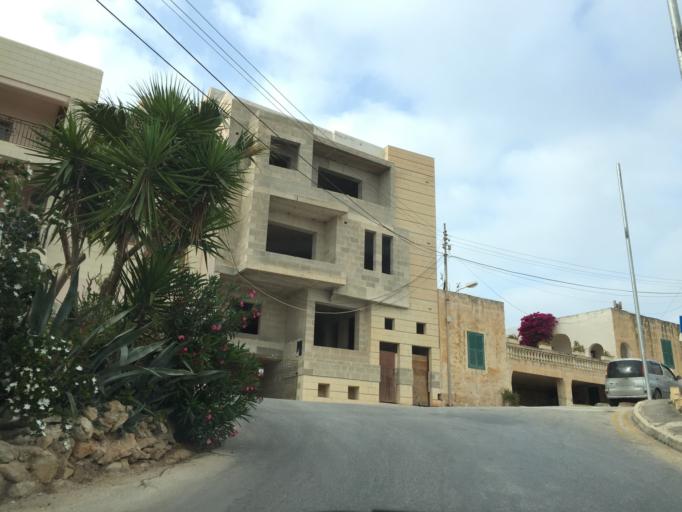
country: MT
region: Il-Mellieha
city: Mellieha
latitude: 35.9406
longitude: 14.3558
